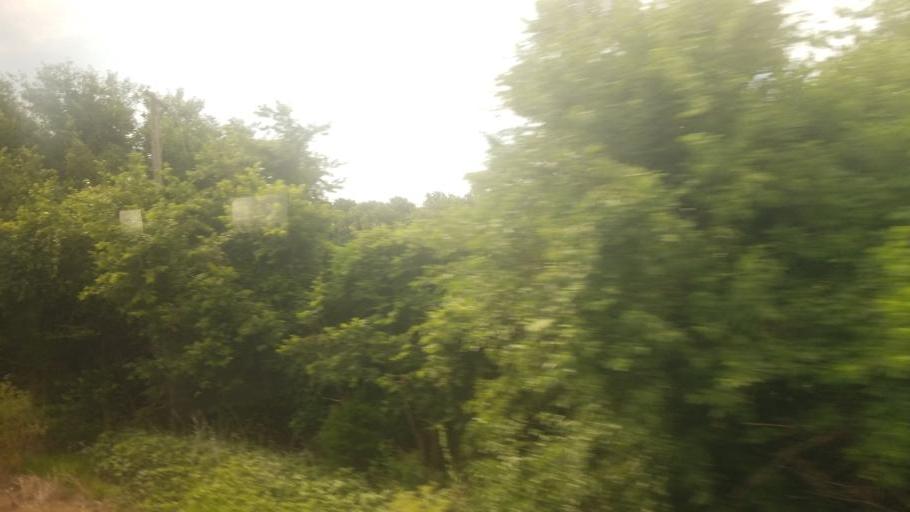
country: US
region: Kansas
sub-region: Douglas County
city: Lawrence
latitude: 38.9500
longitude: -95.1754
